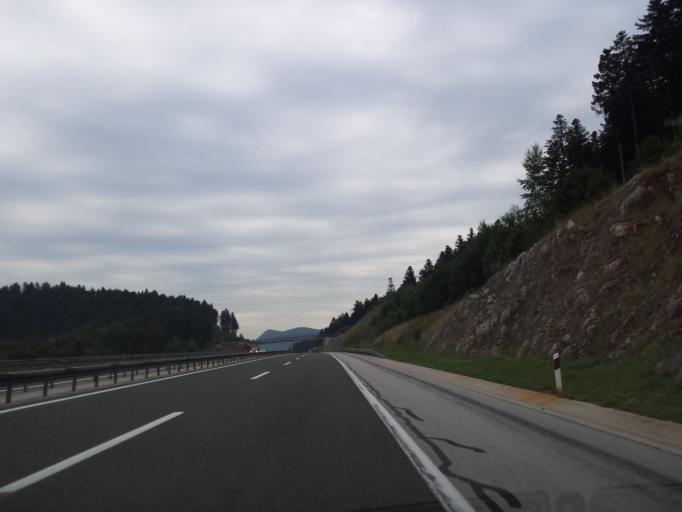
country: HR
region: Licko-Senjska
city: Otocac
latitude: 44.8515
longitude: 15.2285
